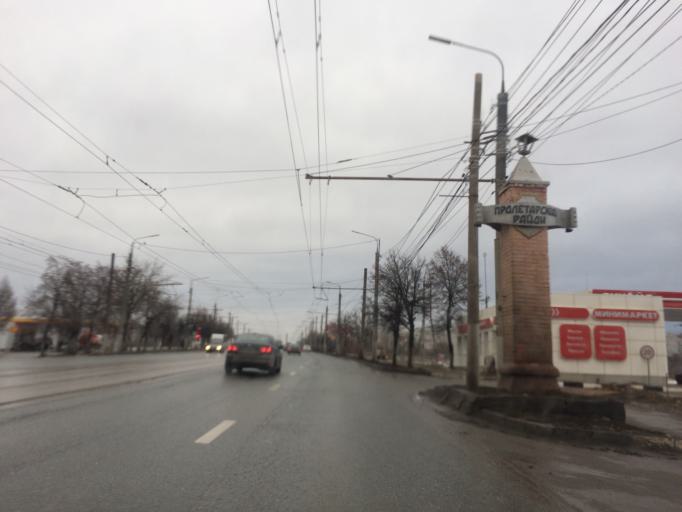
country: RU
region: Tula
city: Tula
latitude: 54.1943
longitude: 37.6311
